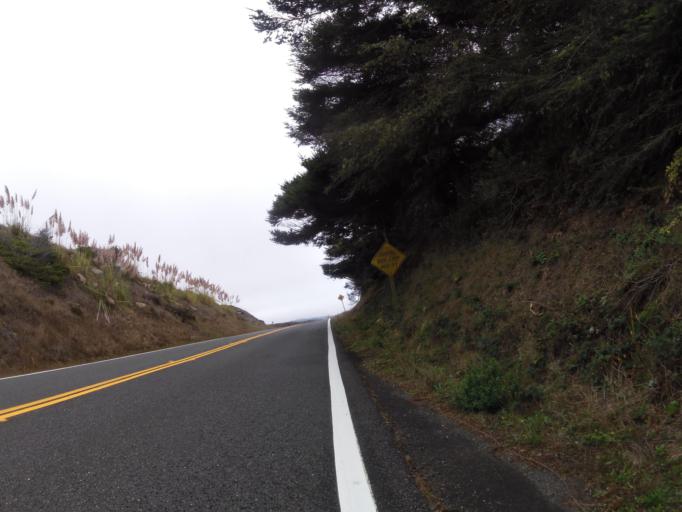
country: US
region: California
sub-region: Sonoma County
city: Monte Rio
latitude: 38.4650
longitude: -123.1515
